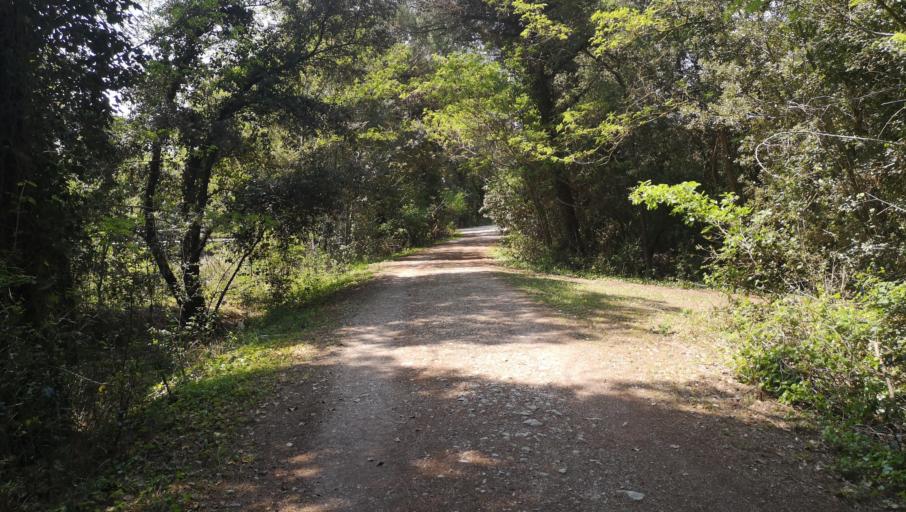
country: IT
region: Emilia-Romagna
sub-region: Provincia di Ravenna
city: Fosso Ghiaia
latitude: 44.3565
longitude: 12.2872
